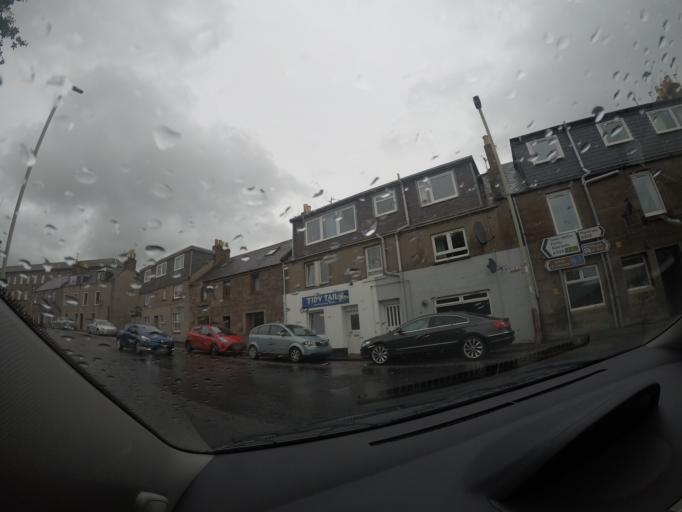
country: GB
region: Scotland
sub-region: Angus
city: Brechin
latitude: 56.7288
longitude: -2.6525
